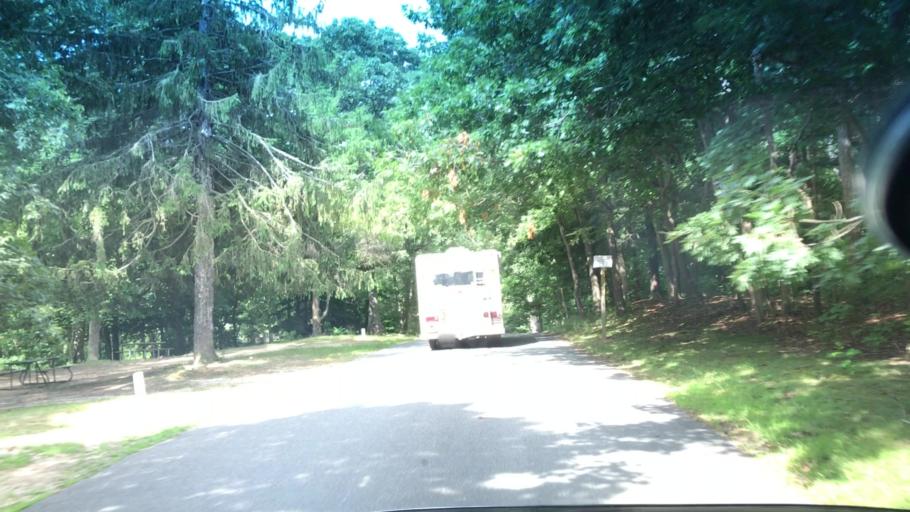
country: US
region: New York
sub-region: Suffolk County
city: Wading River
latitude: 40.9624
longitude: -72.8014
